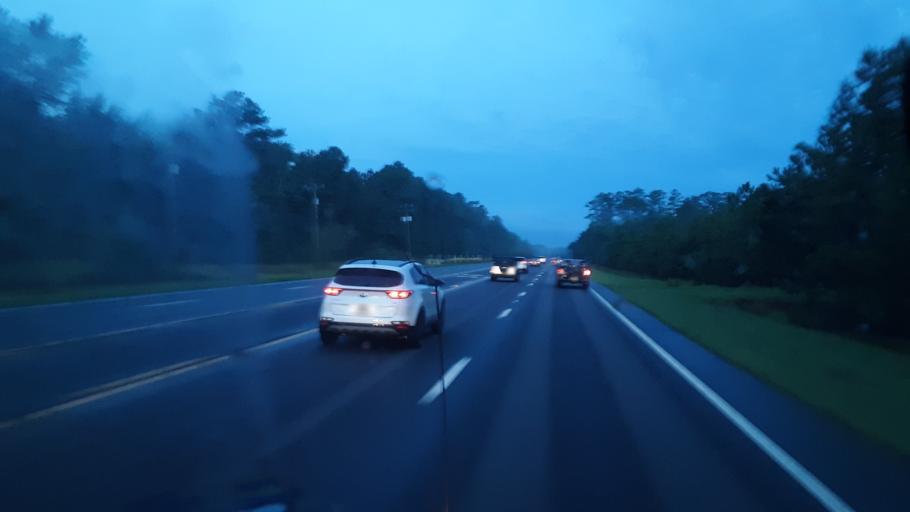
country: US
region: North Carolina
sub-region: Currituck County
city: Currituck
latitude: 36.4544
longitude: -76.0477
